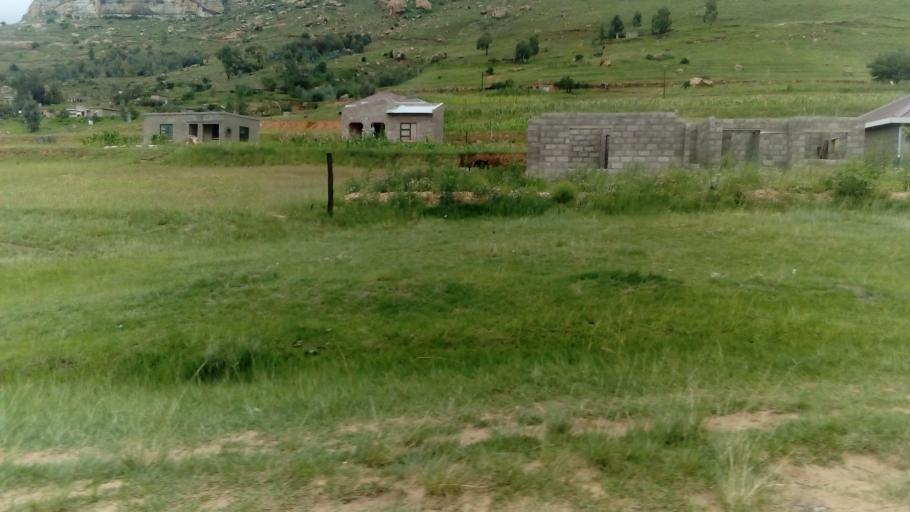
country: LS
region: Leribe
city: Leribe
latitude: -28.9585
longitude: 28.1729
